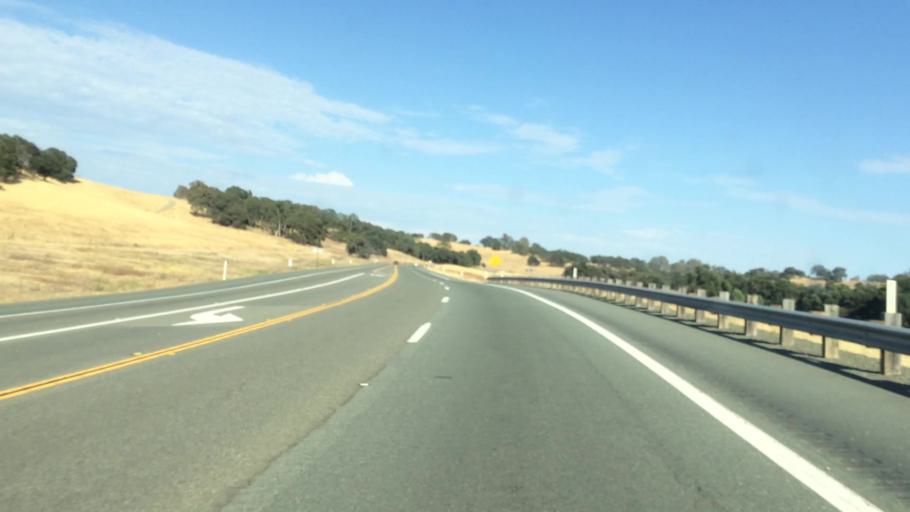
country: US
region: California
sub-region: Amador County
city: Sutter Creek
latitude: 38.4063
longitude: -120.8312
